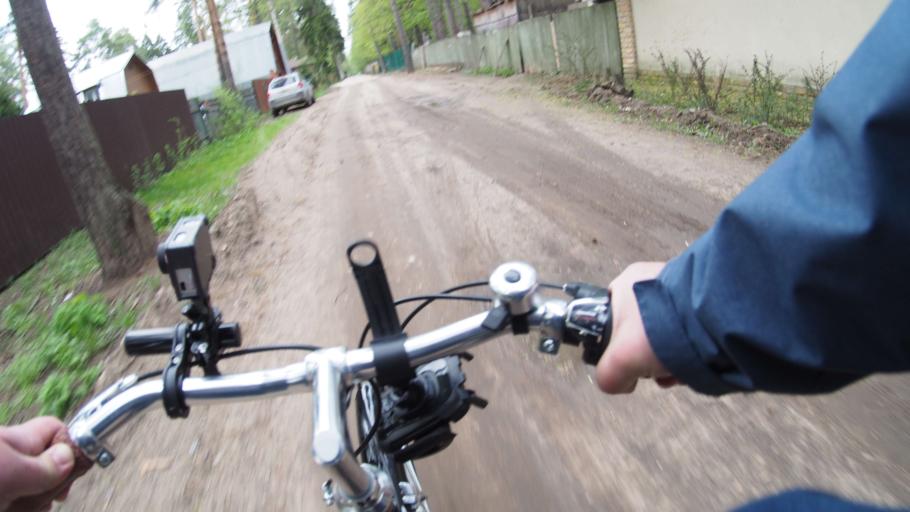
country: RU
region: Moskovskaya
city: Kratovo
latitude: 55.5844
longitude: 38.1867
